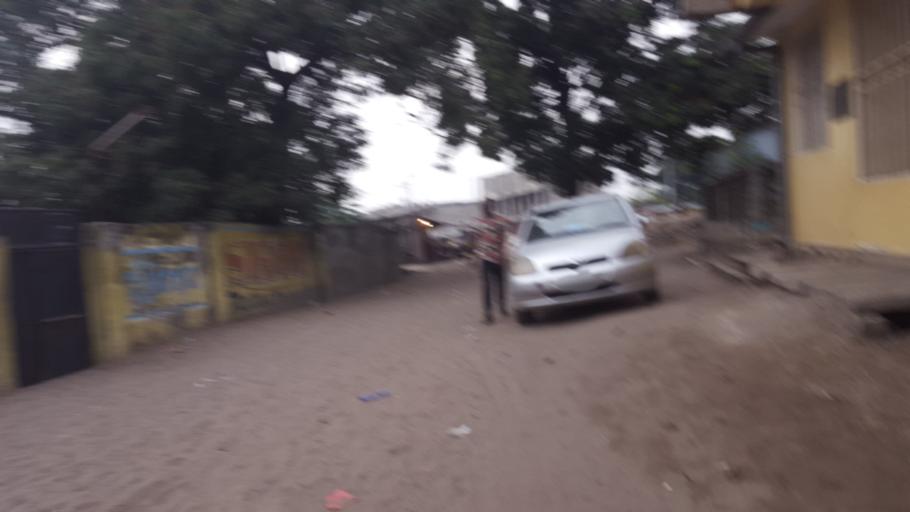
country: CD
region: Kinshasa
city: Masina
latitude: -4.3848
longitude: 15.3562
